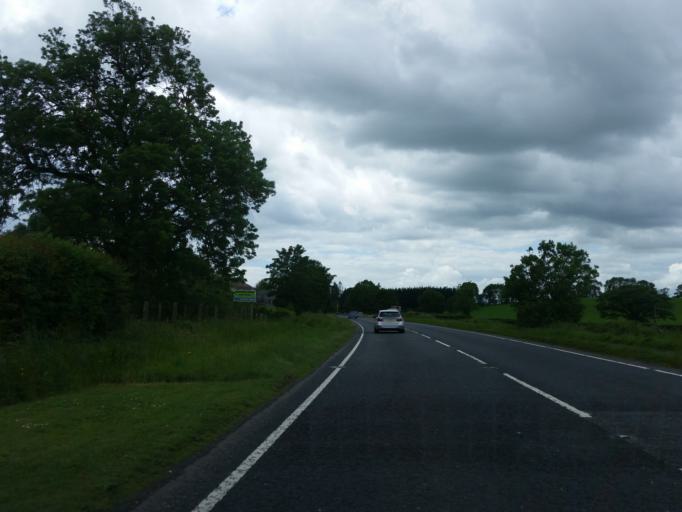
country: GB
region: Northern Ireland
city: Fivemiletown
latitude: 54.4225
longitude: -7.1433
